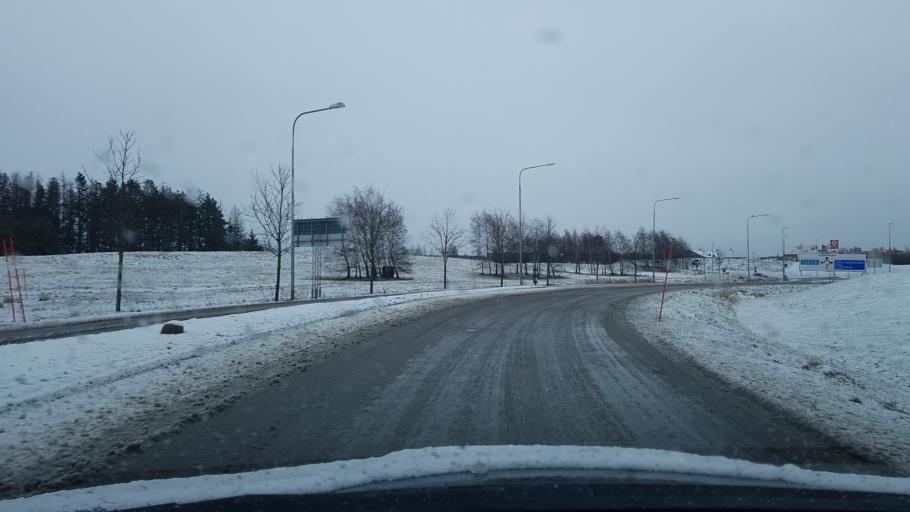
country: SE
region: Uppsala
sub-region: Uppsala Kommun
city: Gamla Uppsala
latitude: 59.8870
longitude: 17.6617
